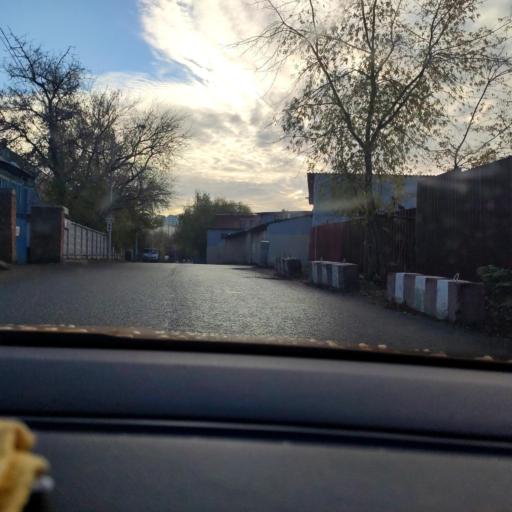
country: RU
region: Moscow
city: Mikhalkovo
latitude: 55.6848
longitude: 37.4393
